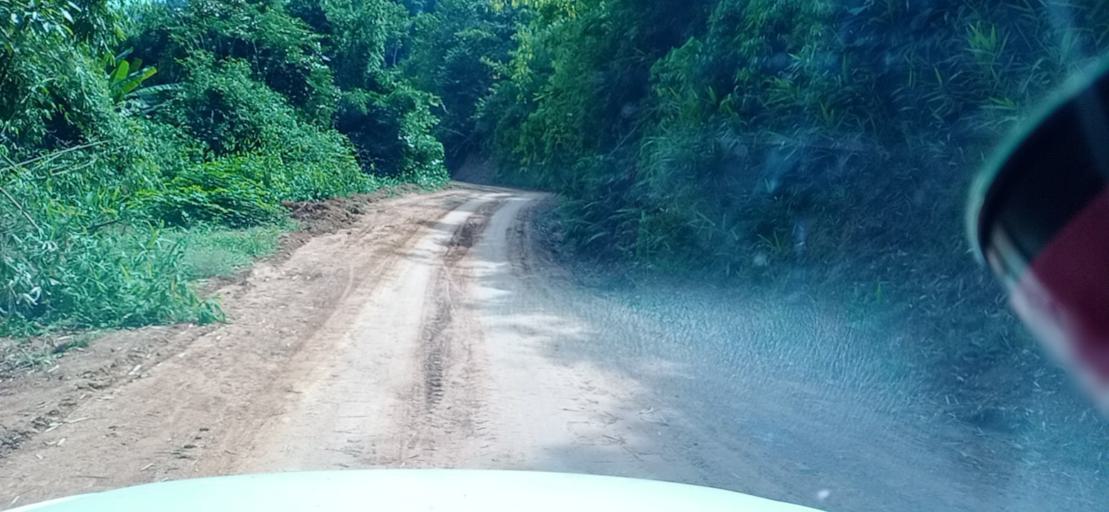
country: TH
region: Changwat Bueng Kan
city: Pak Khat
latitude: 18.6339
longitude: 103.2617
